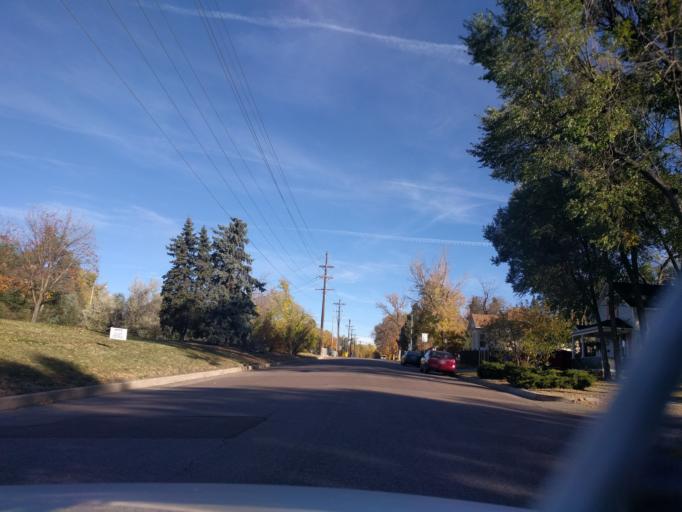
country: US
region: Colorado
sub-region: El Paso County
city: Colorado Springs
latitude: 38.8370
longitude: -104.8129
